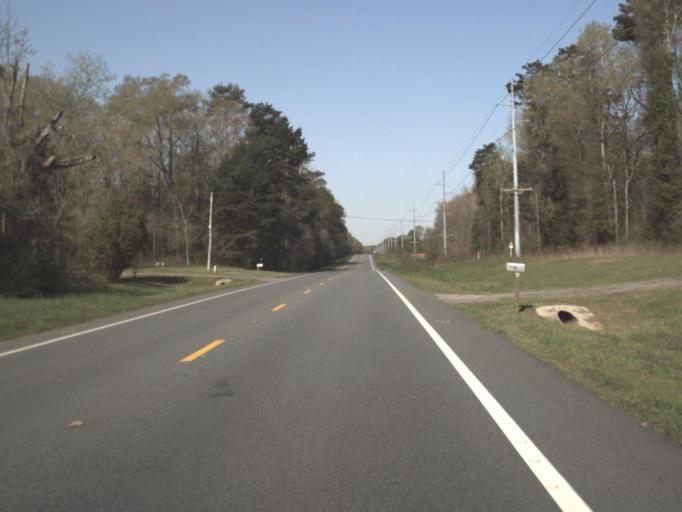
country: US
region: Alabama
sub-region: Houston County
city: Cottonwood
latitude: 30.9348
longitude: -85.3043
